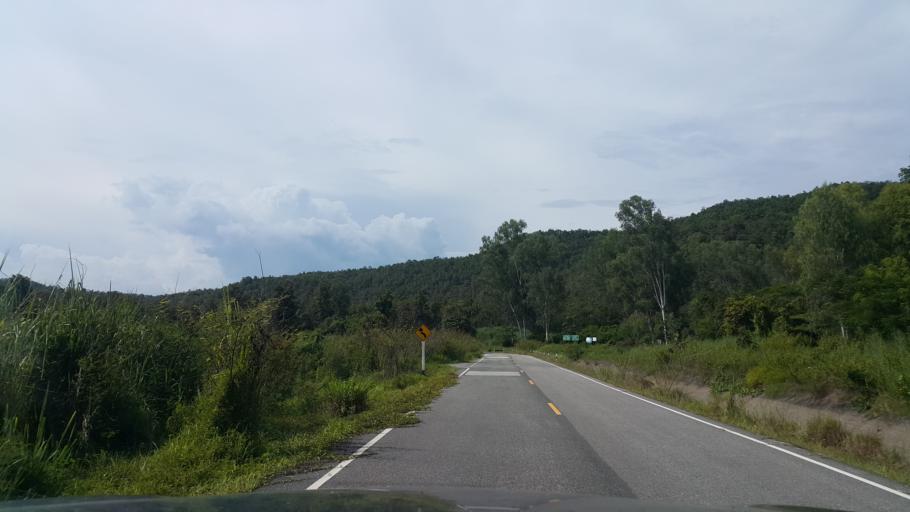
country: TH
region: Chiang Mai
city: Mae On
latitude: 18.8065
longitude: 99.1956
